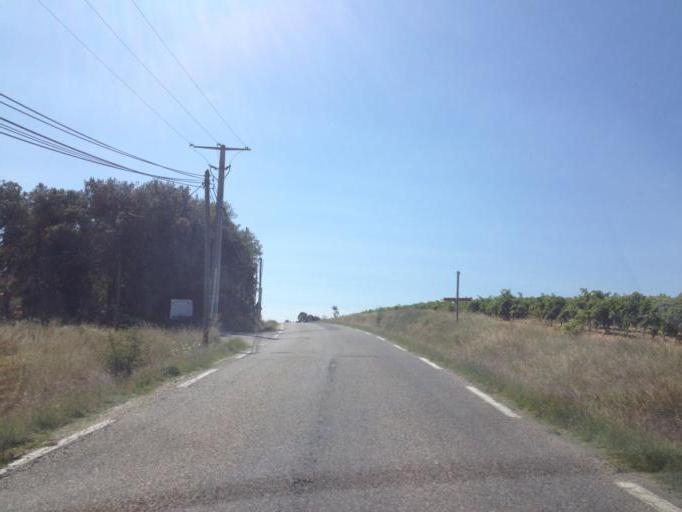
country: FR
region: Provence-Alpes-Cote d'Azur
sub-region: Departement du Vaucluse
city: Orange
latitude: 44.1062
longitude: 4.8201
